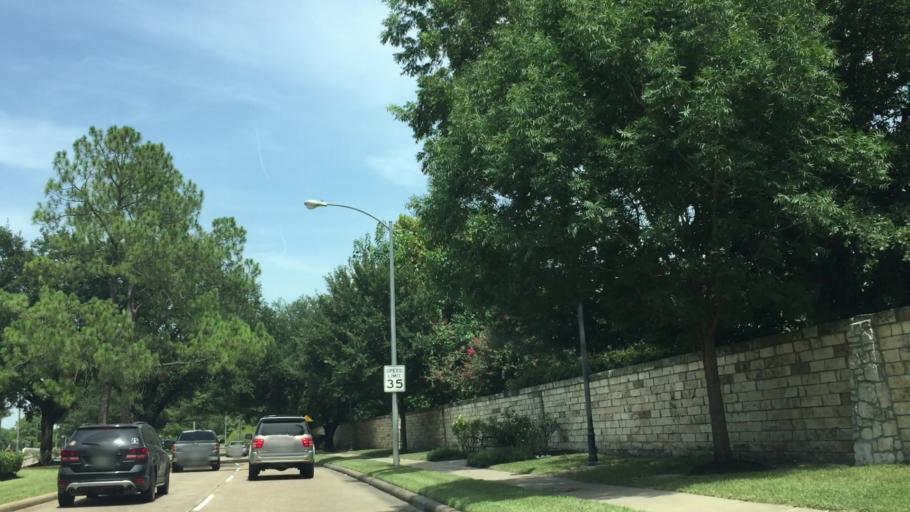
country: US
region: Texas
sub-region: Harris County
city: Jersey Village
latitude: 29.9087
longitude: -95.5723
